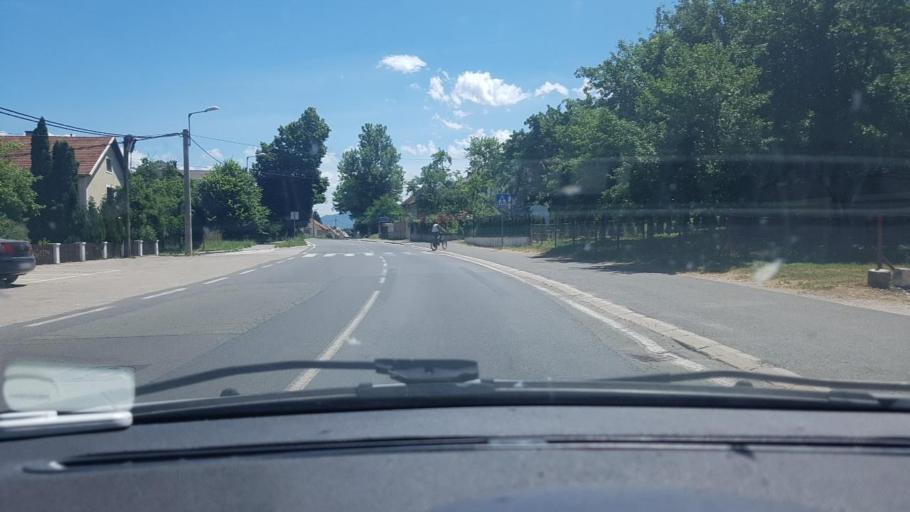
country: HR
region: Licko-Senjska
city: Otocac
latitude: 44.8686
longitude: 15.2454
